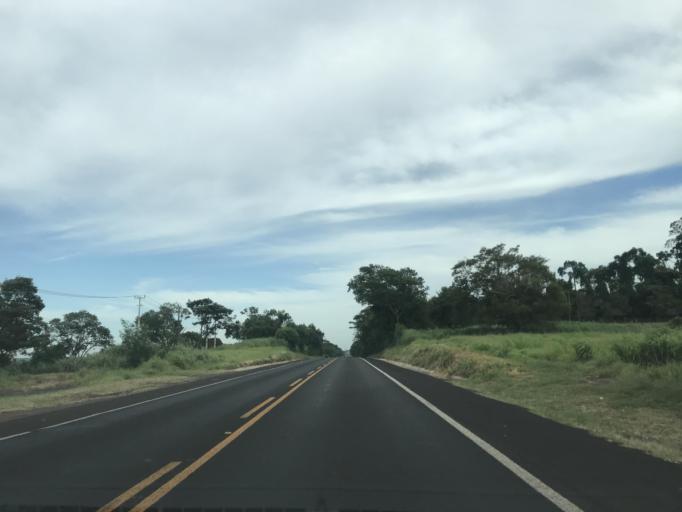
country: BR
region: Parana
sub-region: Paranavai
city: Paranavai
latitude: -23.0236
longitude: -52.4922
